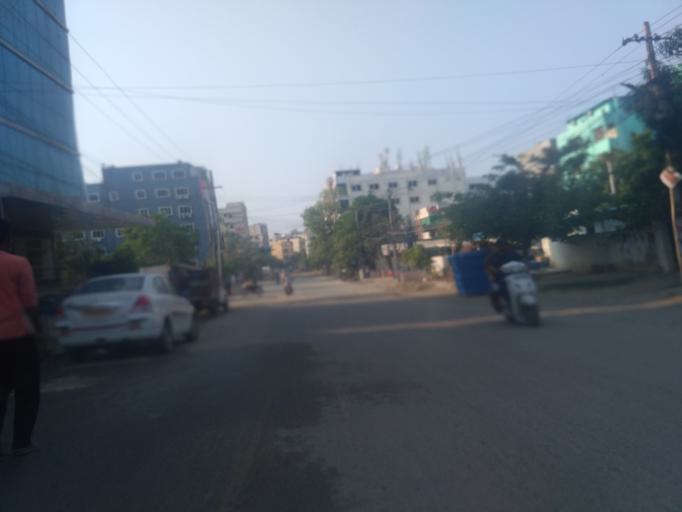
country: IN
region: Telangana
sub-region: Rangareddi
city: Kukatpalli
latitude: 17.4474
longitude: 78.3921
